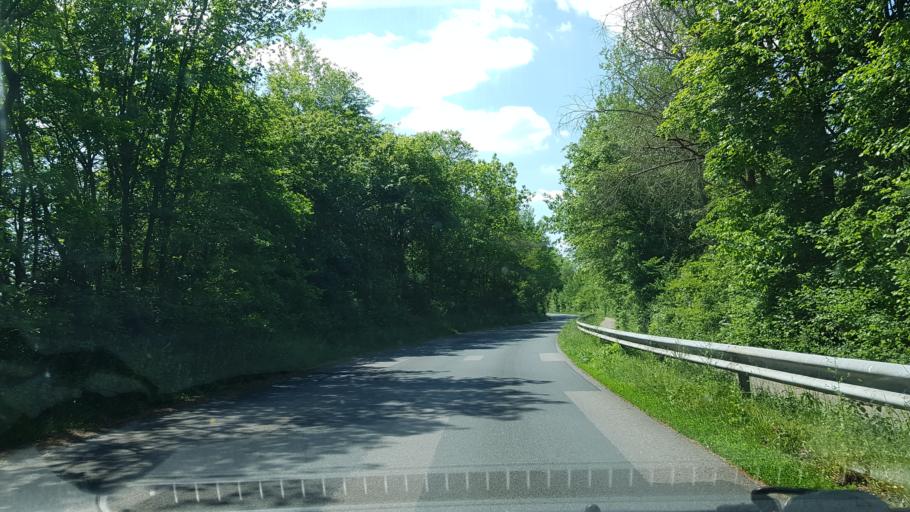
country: DE
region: Lower Saxony
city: Eschede
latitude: 52.7404
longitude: 10.2351
